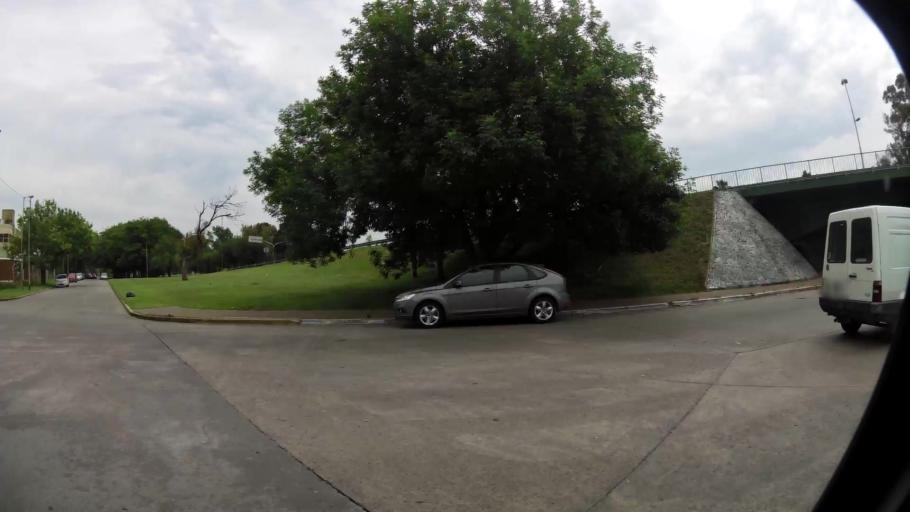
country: AR
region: Buenos Aires
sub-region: Partido de La Plata
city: La Plata
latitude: -34.8974
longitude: -57.9784
